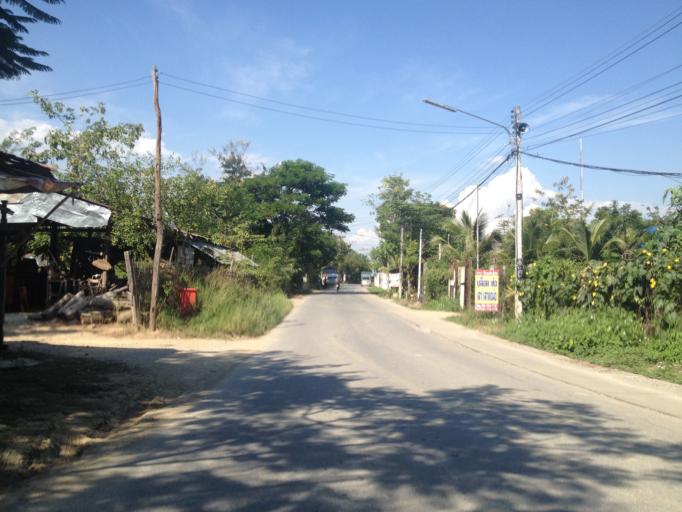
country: TH
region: Chiang Mai
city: Hang Dong
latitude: 18.7039
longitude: 98.9655
